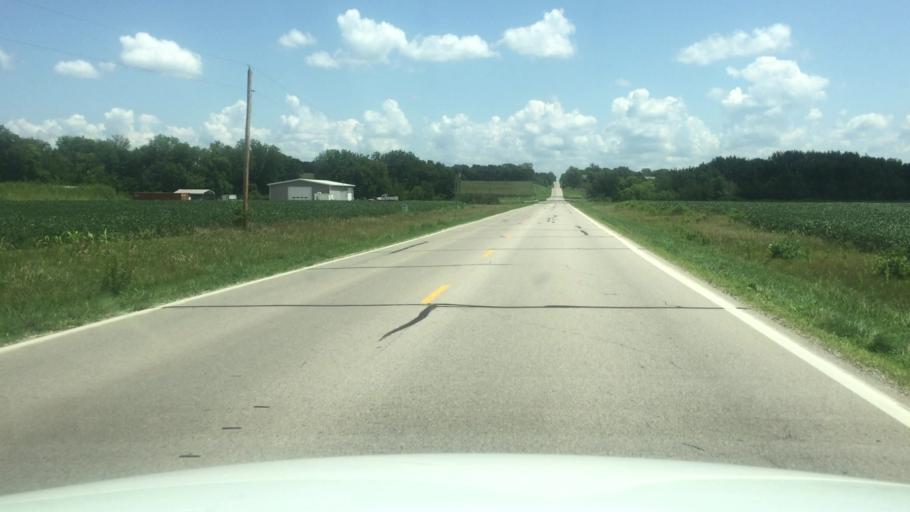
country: US
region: Kansas
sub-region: Brown County
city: Horton
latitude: 39.6673
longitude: -95.5513
